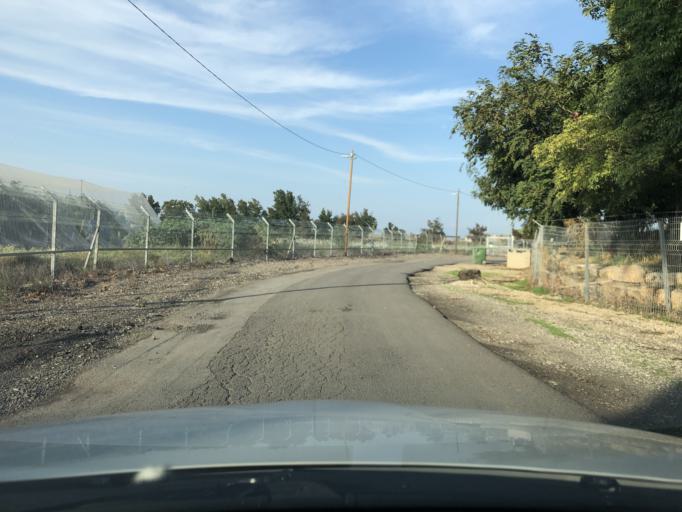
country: IL
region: Northern District
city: Yavne'el
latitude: 32.6631
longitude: 35.5800
